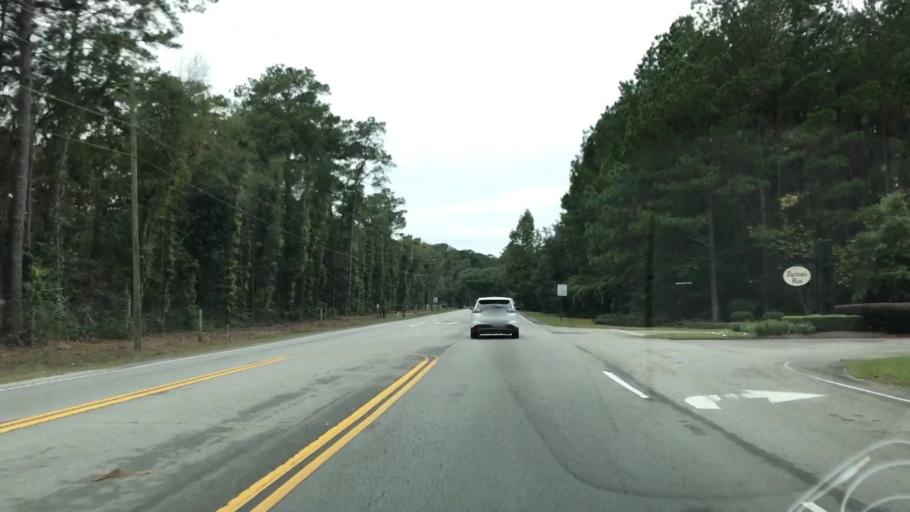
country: US
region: South Carolina
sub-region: Beaufort County
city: Bluffton
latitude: 32.2327
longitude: -80.9056
